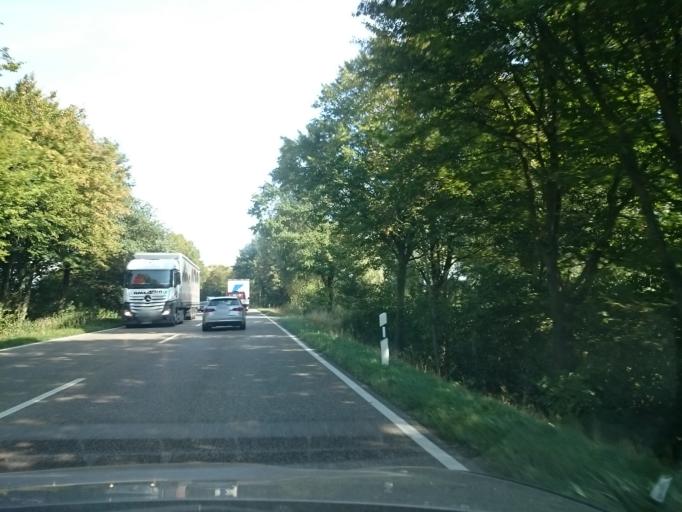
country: DE
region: Bavaria
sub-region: Upper Bavaria
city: Pornbach
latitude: 48.5908
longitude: 11.4063
